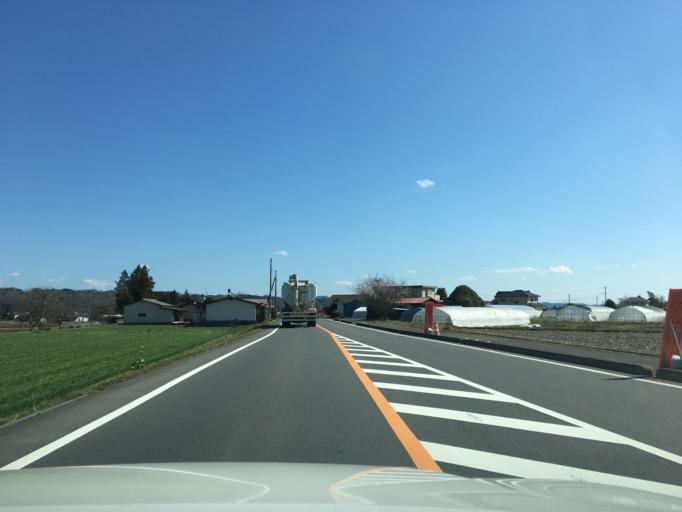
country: JP
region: Tochigi
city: Otawara
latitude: 36.7780
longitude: 140.1192
